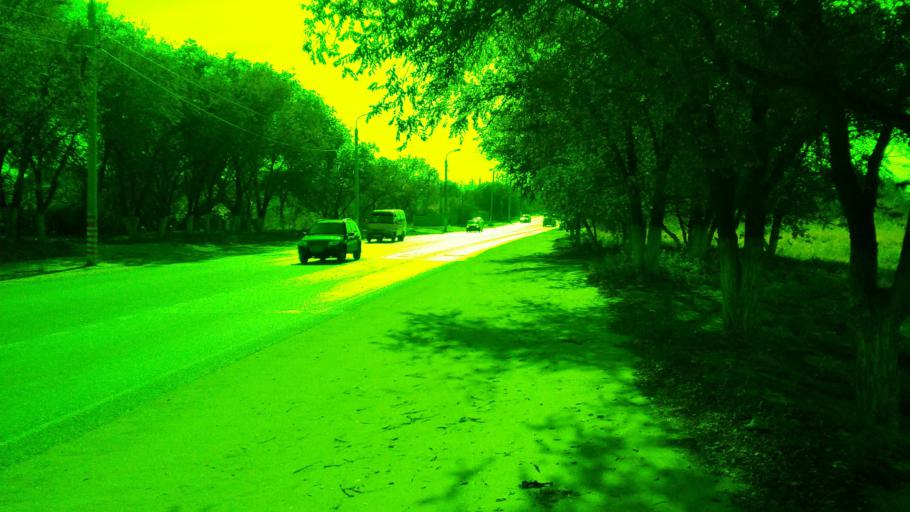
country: RU
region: Volgograd
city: Vodstroy
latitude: 48.8372
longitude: 44.6461
